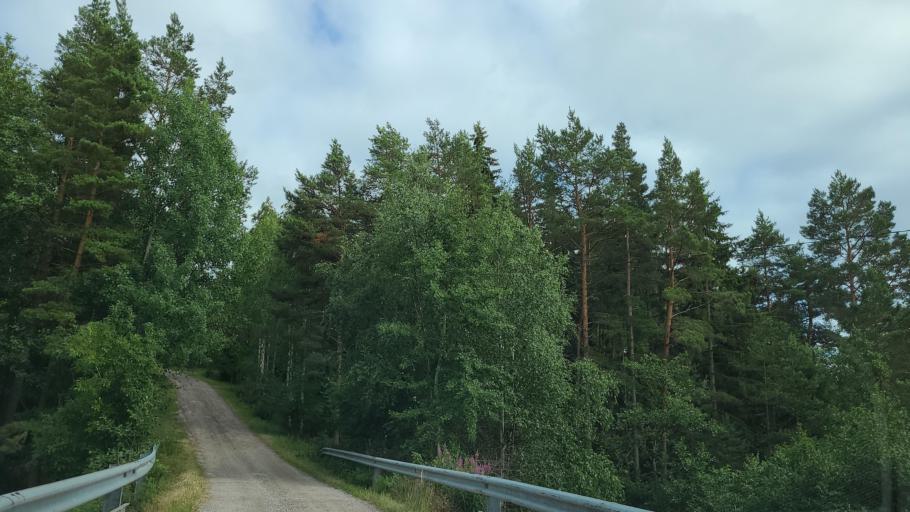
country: FI
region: Varsinais-Suomi
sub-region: Aboland-Turunmaa
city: Nagu
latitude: 60.1303
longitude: 21.7983
